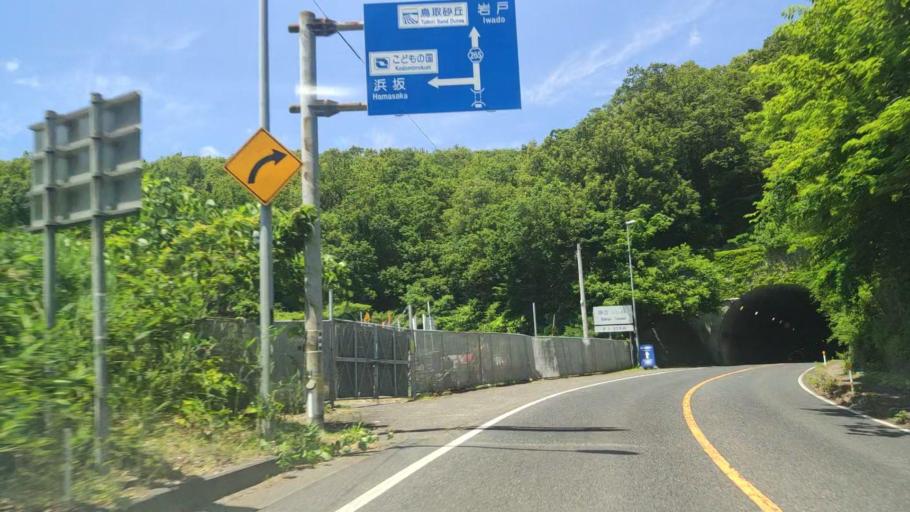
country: JP
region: Tottori
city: Tottori
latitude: 35.5301
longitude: 134.2290
